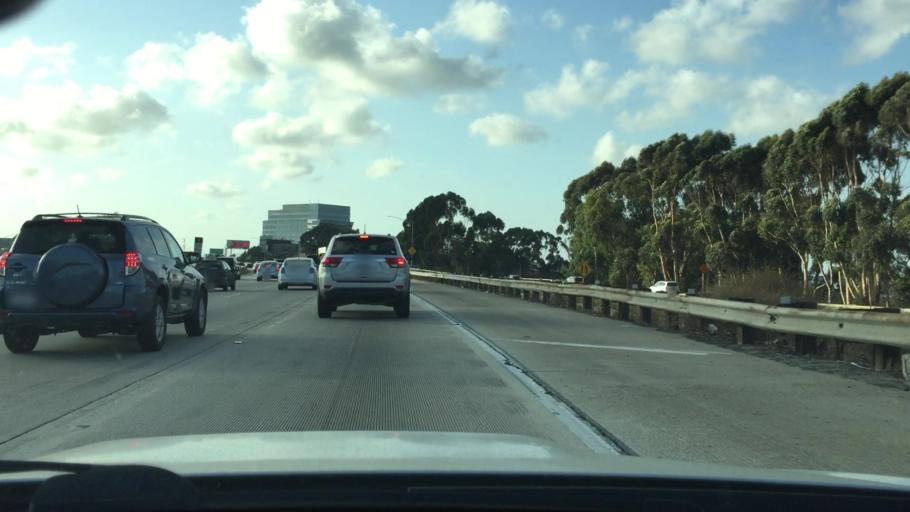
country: US
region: California
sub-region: Los Angeles County
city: Carson
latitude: 33.8561
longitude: -118.2835
